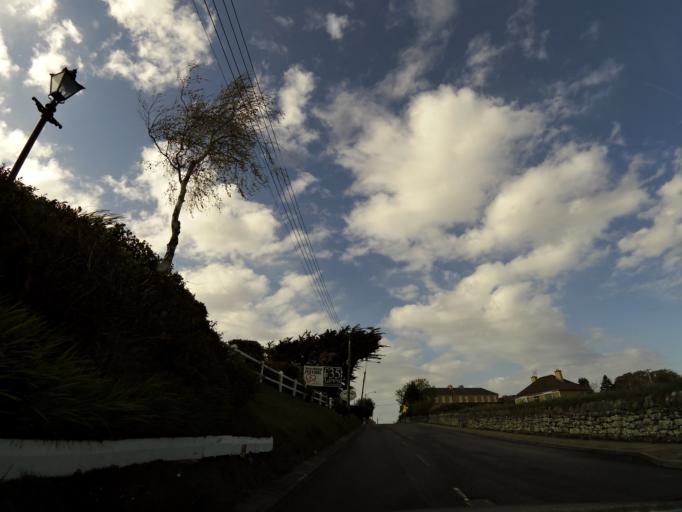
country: IE
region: Connaught
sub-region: County Galway
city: Bearna
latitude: 53.0266
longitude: -9.2900
